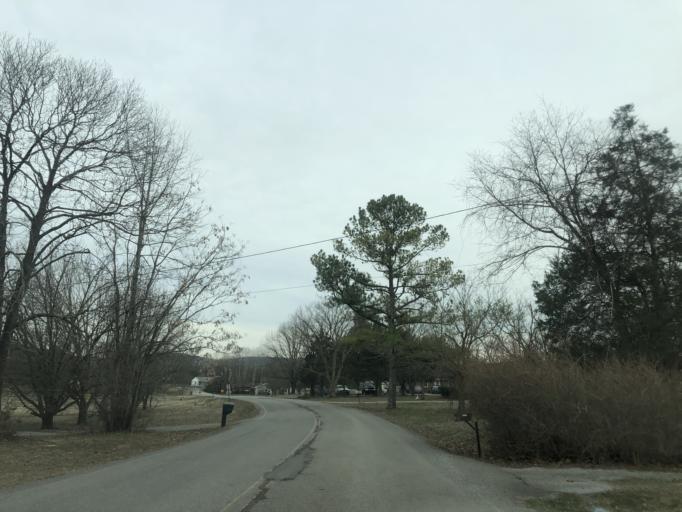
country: US
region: Tennessee
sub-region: Wilson County
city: Lebanon
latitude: 36.2444
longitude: -86.2602
